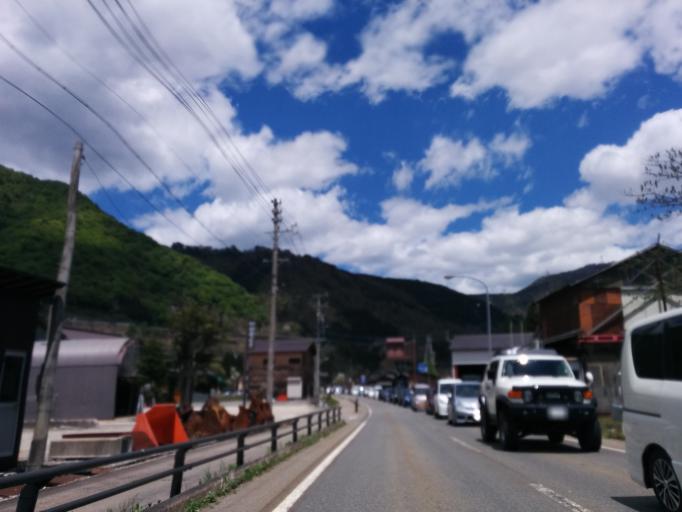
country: JP
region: Toyama
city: Fukumitsu
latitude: 36.2749
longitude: 136.9013
